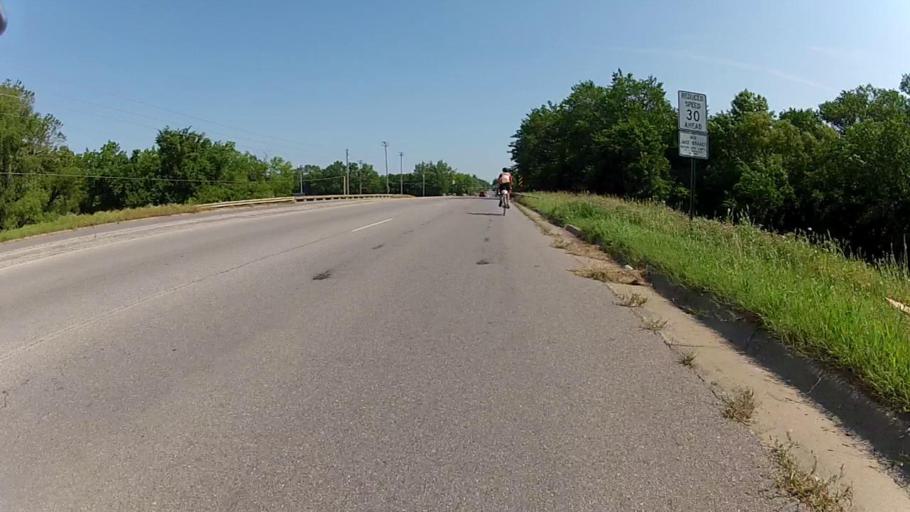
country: US
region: Kansas
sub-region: Montgomery County
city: Independence
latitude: 37.2138
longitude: -95.7108
